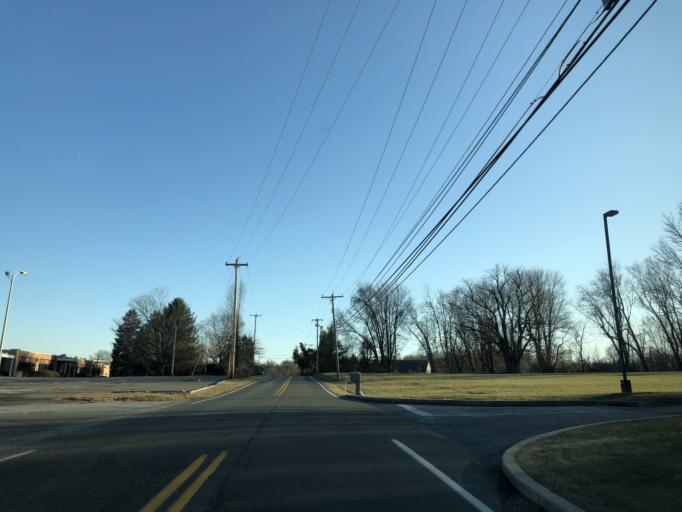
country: US
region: Pennsylvania
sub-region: Delaware County
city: Chester Heights
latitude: 39.8668
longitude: -75.5076
